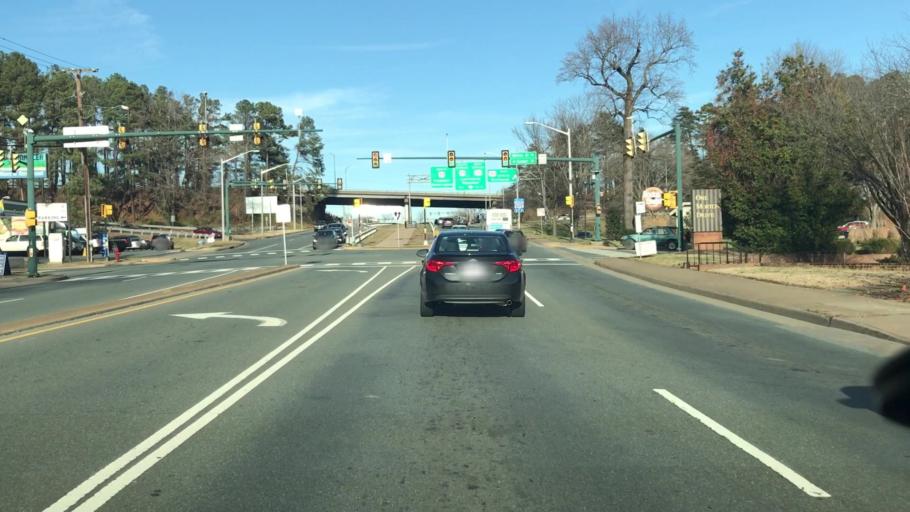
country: US
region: Virginia
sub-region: City of Charlottesville
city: Charlottesville
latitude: 38.0556
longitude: -78.4967
